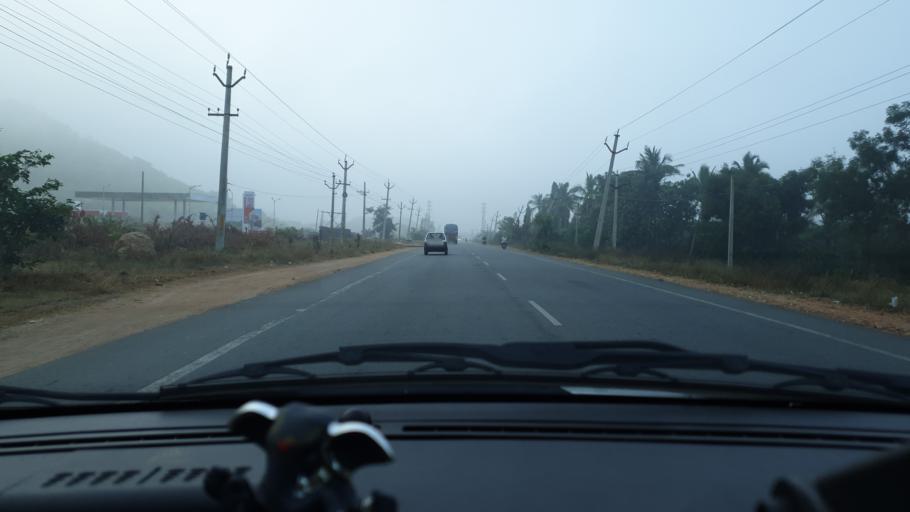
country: IN
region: Telangana
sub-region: Mahbubnagar
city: Farrukhnagar
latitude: 16.8681
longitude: 78.5293
